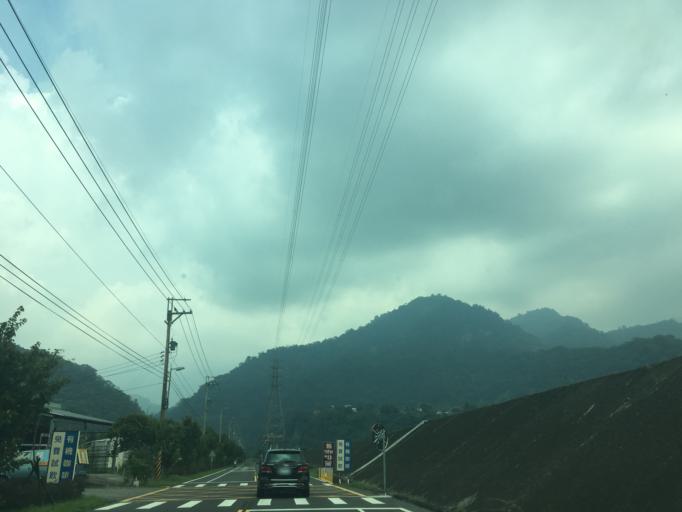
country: TW
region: Taiwan
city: Fengyuan
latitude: 24.2946
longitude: 120.9000
